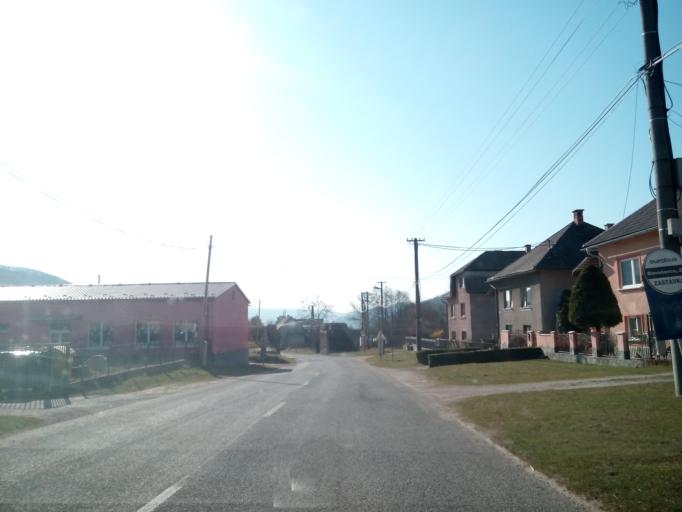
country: SK
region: Kosicky
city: Dobsina
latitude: 48.7140
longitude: 20.2785
